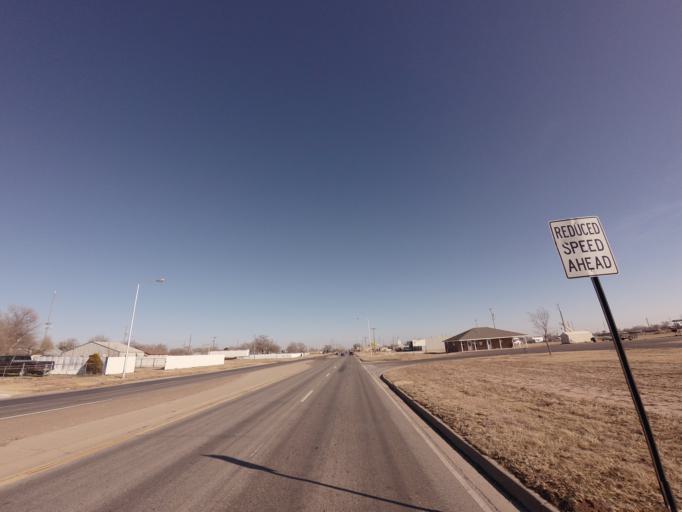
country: US
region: New Mexico
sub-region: Curry County
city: Clovis
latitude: 34.4007
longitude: -103.2352
